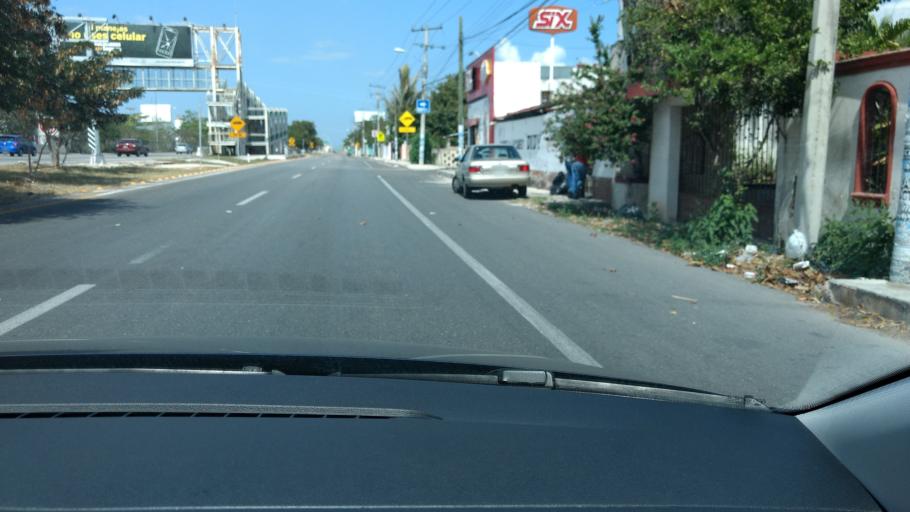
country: MX
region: Yucatan
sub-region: Kanasin
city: Kanasin
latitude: 20.9737
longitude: -89.5647
